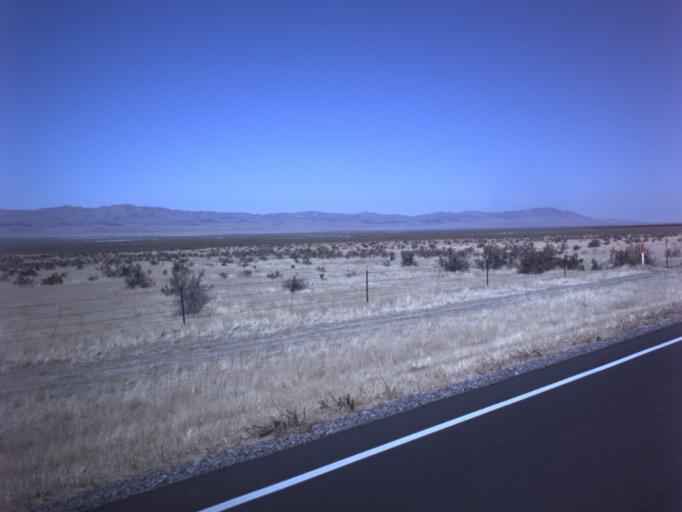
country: US
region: Utah
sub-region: Tooele County
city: Grantsville
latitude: 40.4615
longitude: -112.7472
